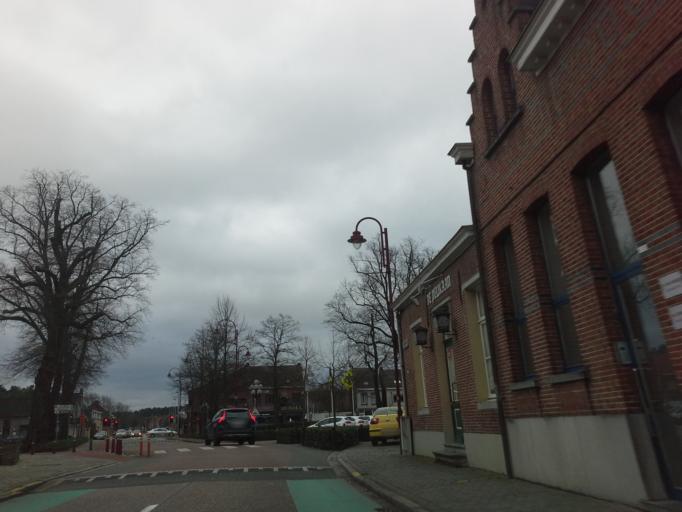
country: BE
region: Flanders
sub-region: Provincie Antwerpen
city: Olen
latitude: 51.1441
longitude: 4.8584
